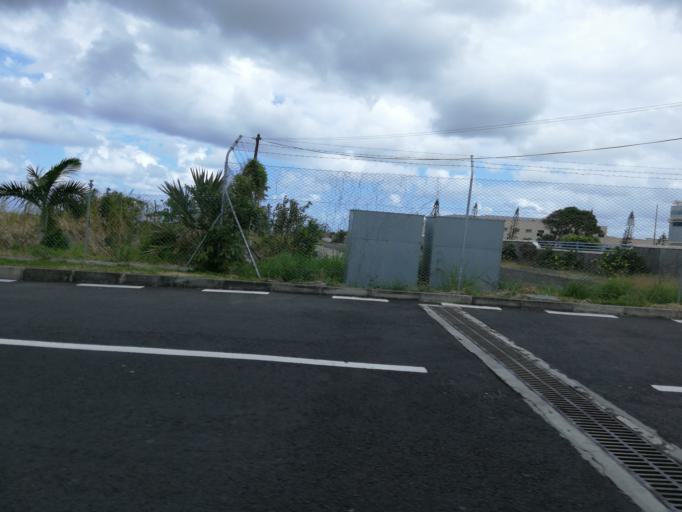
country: MU
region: Grand Port
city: Plaine Magnien
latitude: -20.4354
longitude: 57.6765
